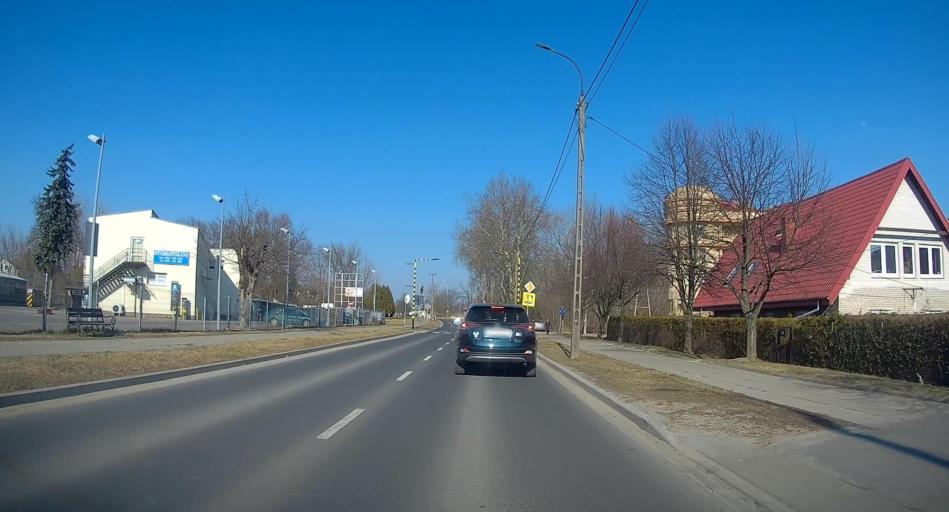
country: PL
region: Masovian Voivodeship
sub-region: Powiat piaseczynski
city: Konstancin-Jeziorna
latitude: 52.0967
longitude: 21.1232
